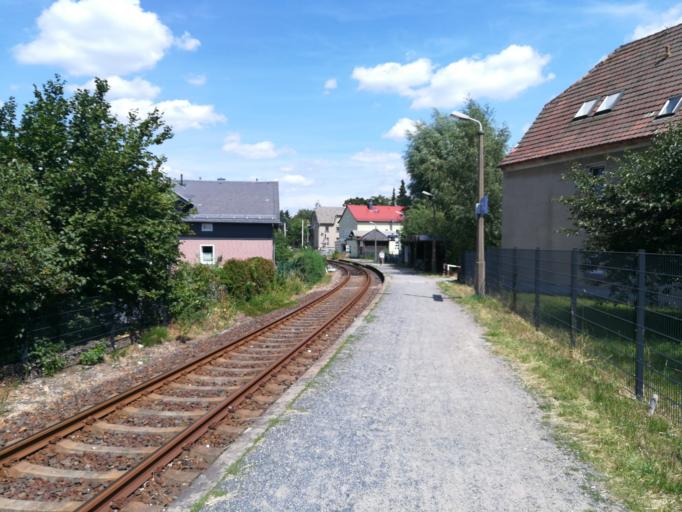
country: DE
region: Saxony
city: Ottendorf-Okrilla
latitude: 51.1865
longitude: 13.8355
